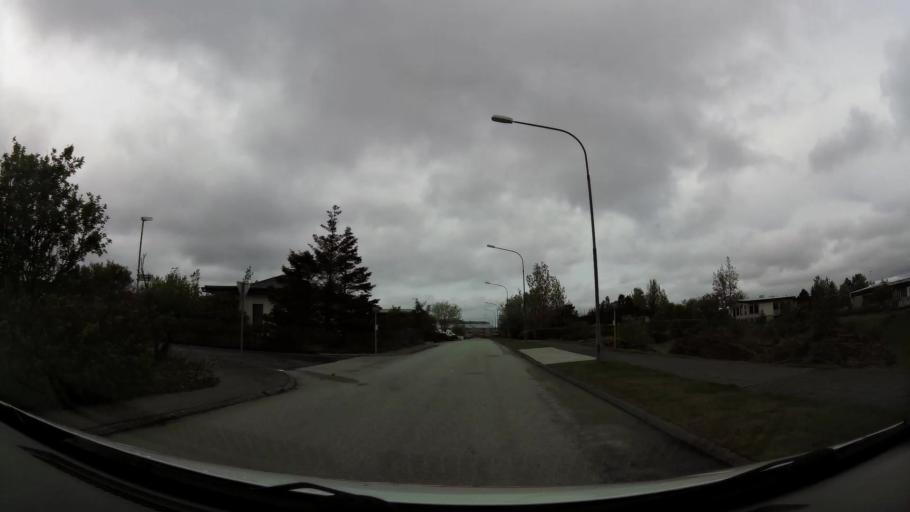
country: IS
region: Capital Region
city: Hafnarfjoerdur
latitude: 64.0778
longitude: -21.9665
